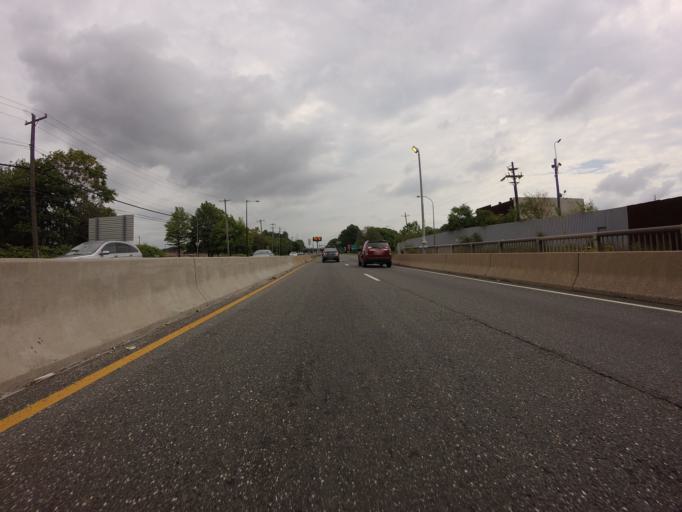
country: US
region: New Jersey
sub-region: Gloucester County
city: National Park
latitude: 39.9042
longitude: -75.1972
